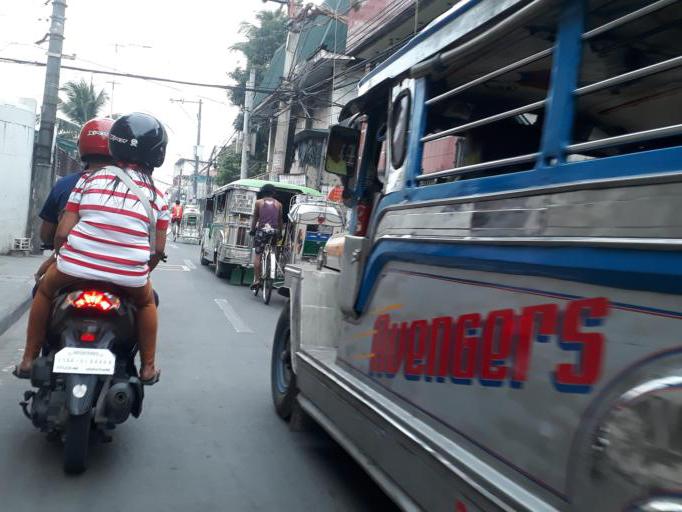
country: PH
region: Calabarzon
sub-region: Province of Rizal
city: Navotas
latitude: 14.6609
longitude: 120.9443
